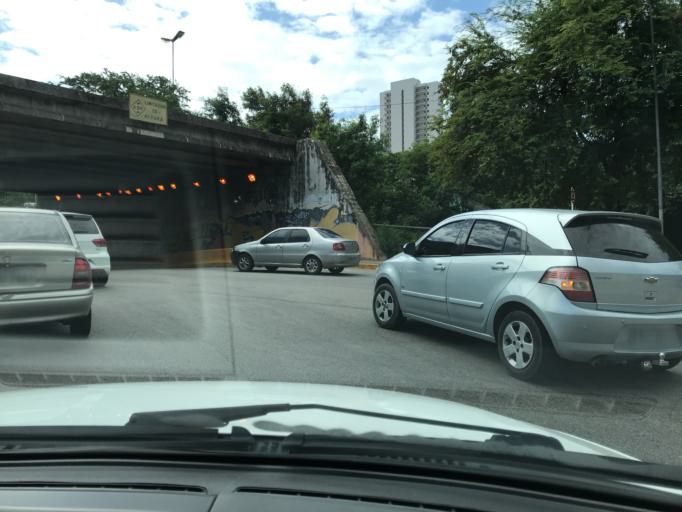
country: BR
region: Pernambuco
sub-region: Recife
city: Recife
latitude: -8.0622
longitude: -34.9016
